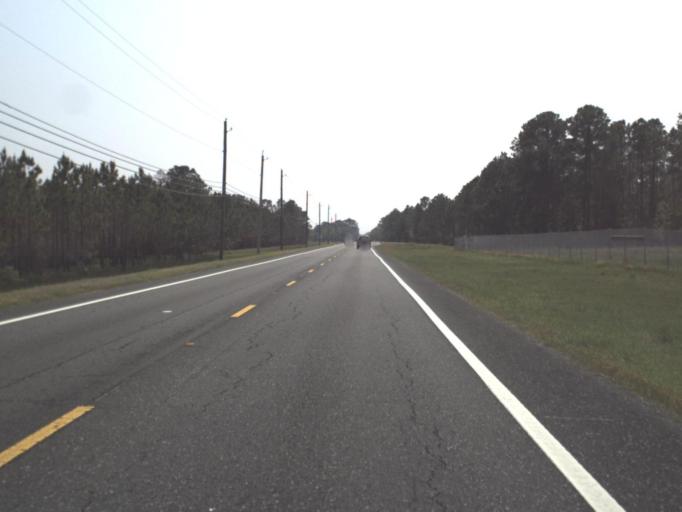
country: US
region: Florida
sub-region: Santa Rosa County
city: Oriole Beach
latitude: 30.4668
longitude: -87.0877
